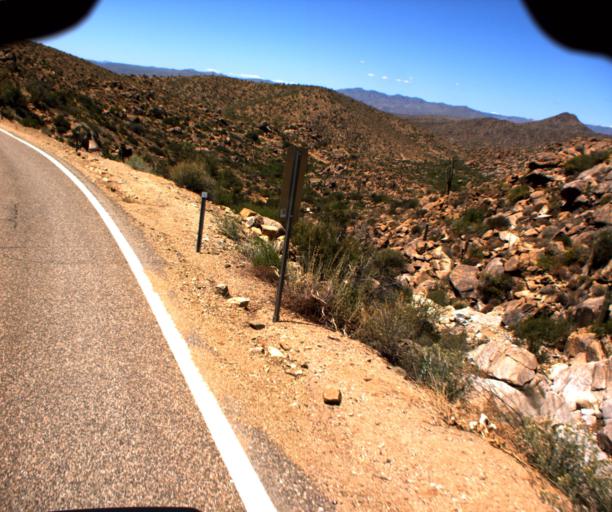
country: US
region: Arizona
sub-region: Yavapai County
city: Bagdad
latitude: 34.4495
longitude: -112.9733
